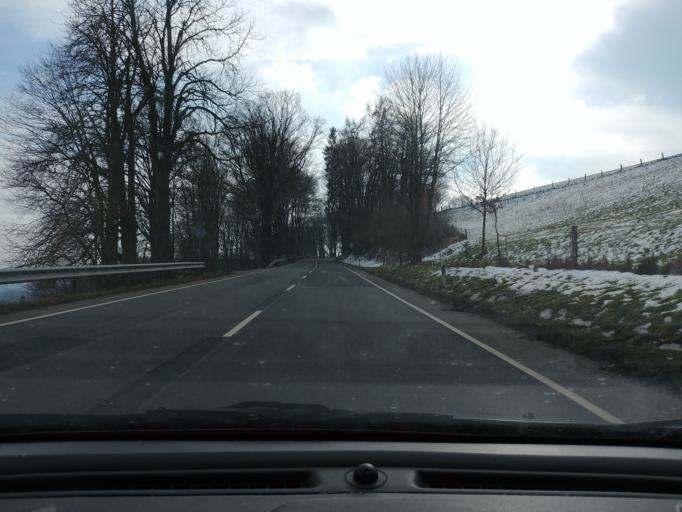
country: DE
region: Lower Saxony
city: Bodenfelde
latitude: 51.6876
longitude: 9.5165
